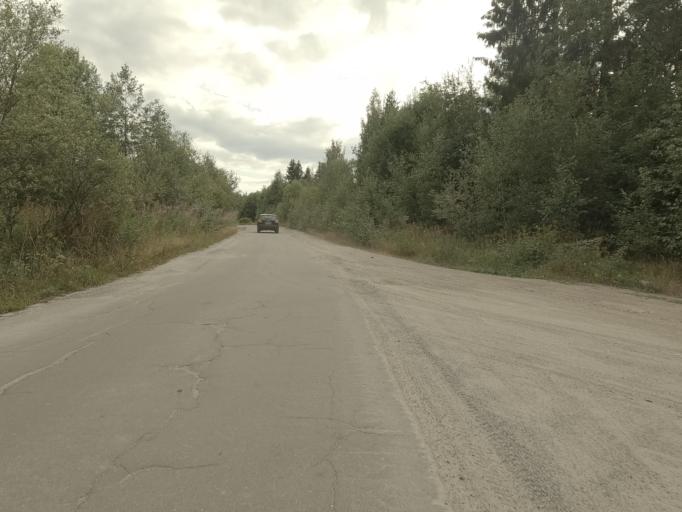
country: RU
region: Leningrad
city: Kamennogorsk
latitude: 60.9696
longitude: 29.1386
